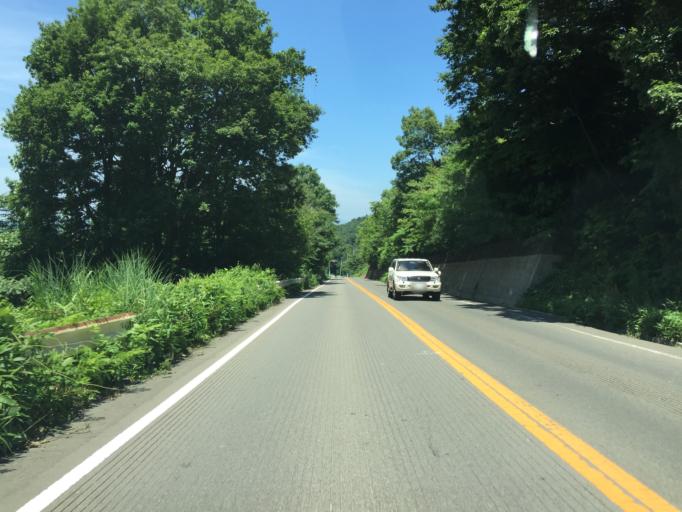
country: JP
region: Fukushima
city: Fukushima-shi
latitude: 37.7531
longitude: 140.5214
